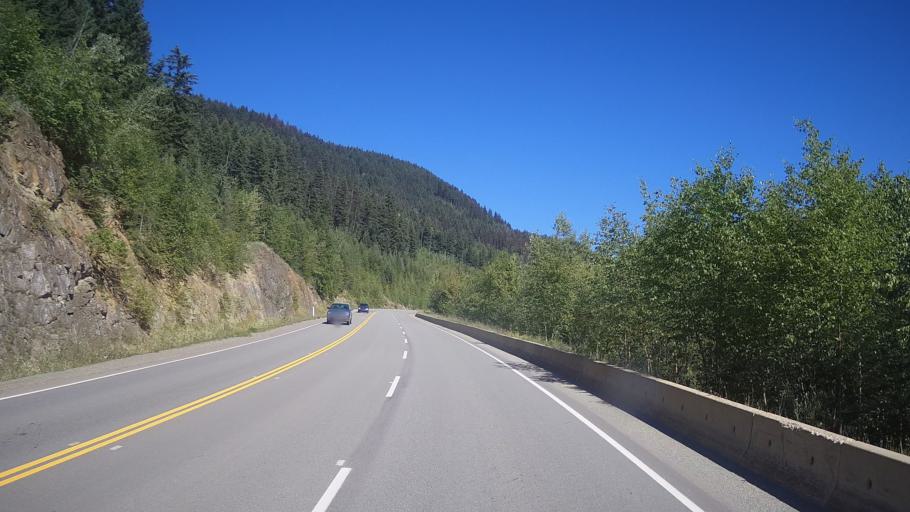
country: CA
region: British Columbia
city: Kamloops
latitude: 51.4665
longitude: -120.2502
